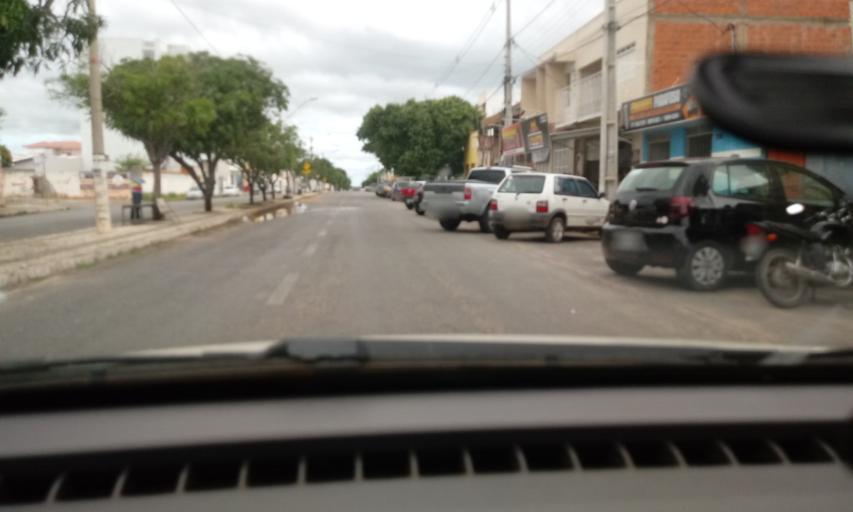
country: BR
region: Bahia
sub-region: Guanambi
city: Guanambi
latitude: -14.2159
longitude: -42.7845
